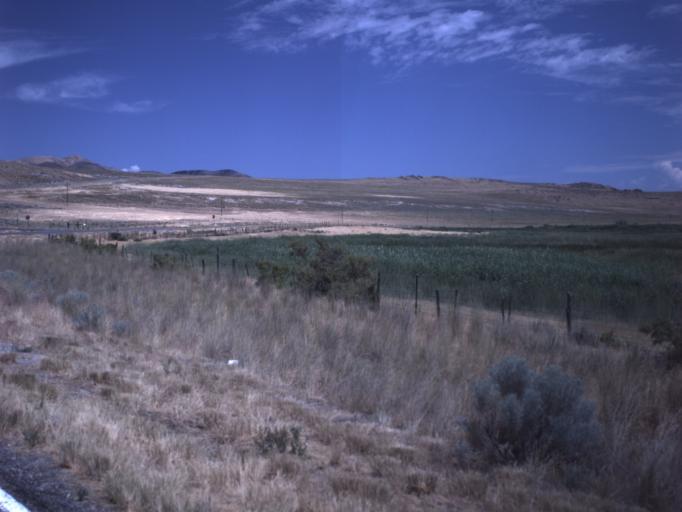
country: US
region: Utah
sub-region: Box Elder County
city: Tremonton
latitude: 41.6163
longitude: -112.3672
